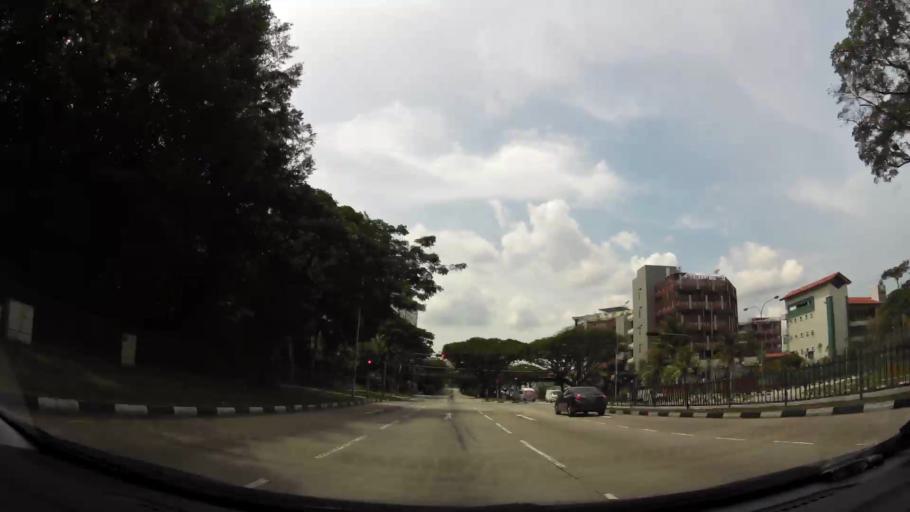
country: MY
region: Johor
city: Johor Bahru
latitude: 1.3501
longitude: 103.7098
